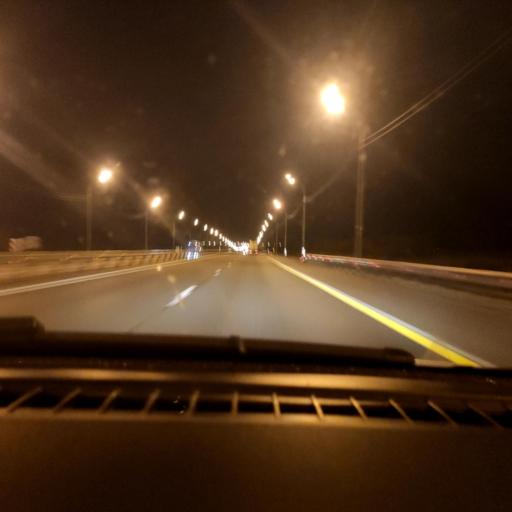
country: RU
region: Lipetsk
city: Khlevnoye
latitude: 52.1990
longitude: 39.1679
